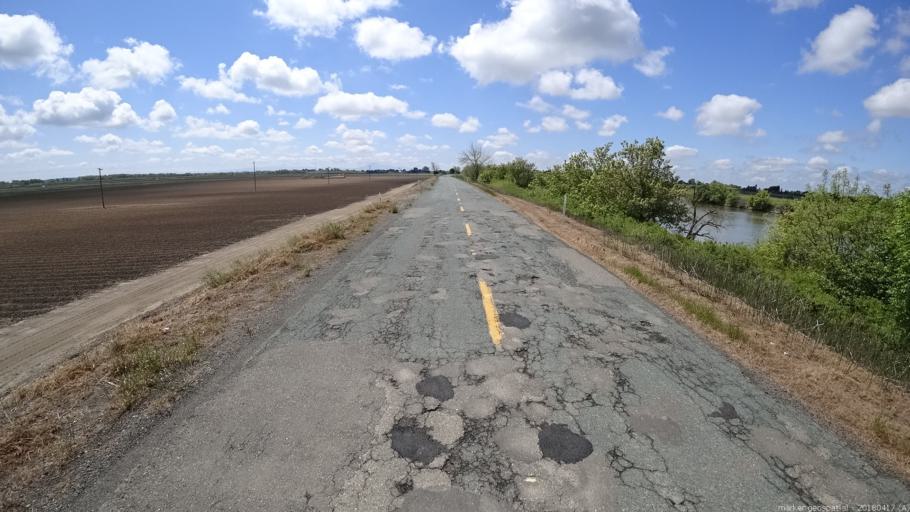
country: US
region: California
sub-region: Sacramento County
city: Walnut Grove
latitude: 38.1840
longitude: -121.5662
